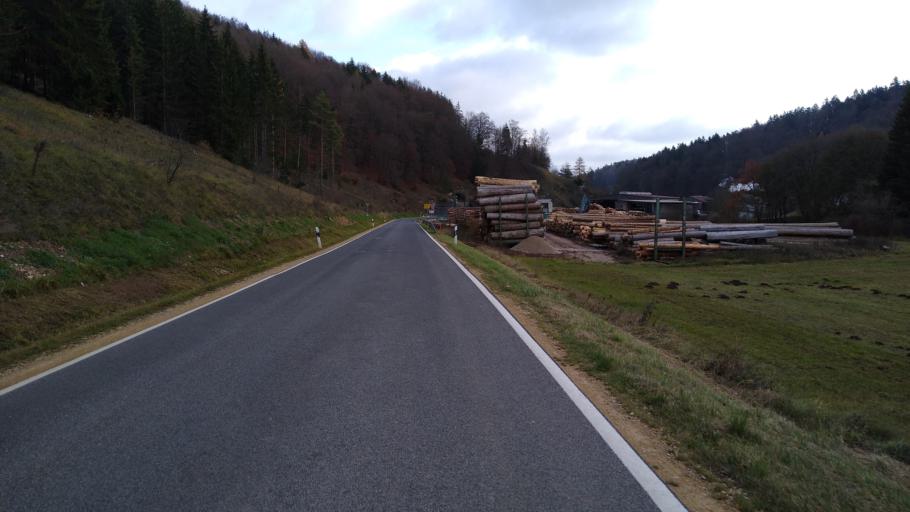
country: DE
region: Bavaria
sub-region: Upper Palatinate
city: Dietfurt
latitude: 49.0887
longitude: 11.6114
